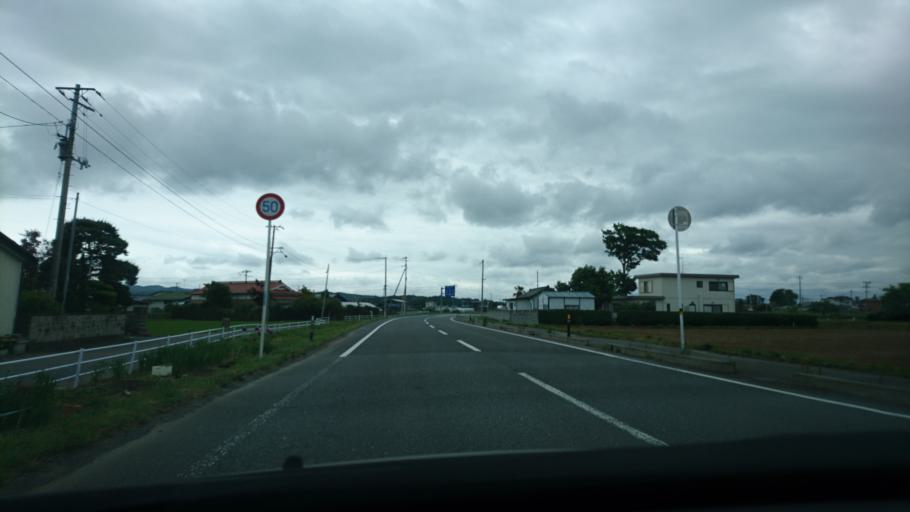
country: JP
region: Miyagi
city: Wakuya
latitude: 38.7104
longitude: 141.2593
